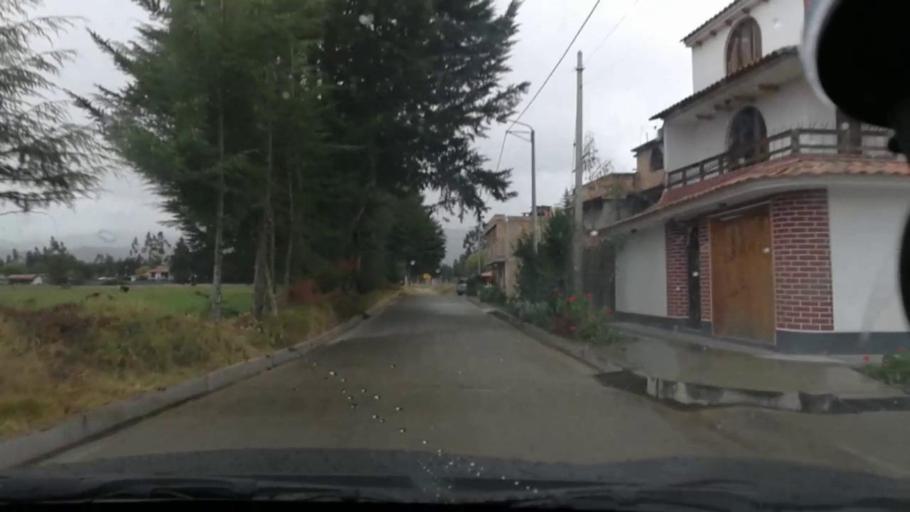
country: PE
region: Cajamarca
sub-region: Provincia de Cajamarca
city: Cajamarca
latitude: -7.1618
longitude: -78.4702
